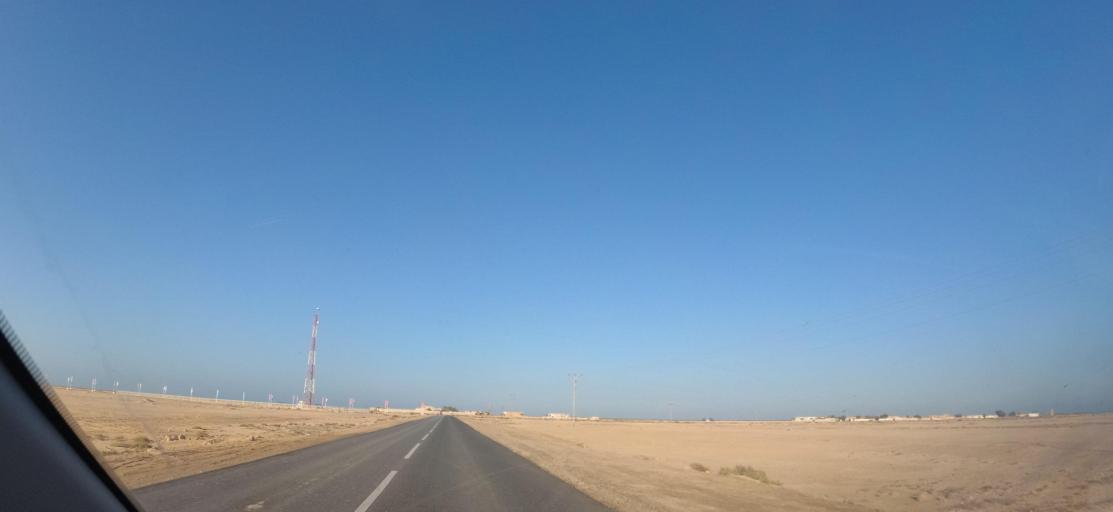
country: QA
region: Madinat ash Shamal
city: Ar Ru'ays
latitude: 26.1517
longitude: 51.2499
